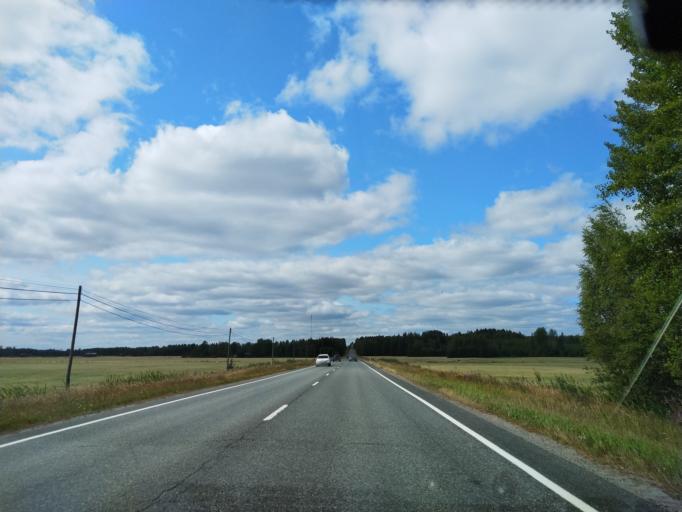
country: FI
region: Haeme
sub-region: Haemeenlinna
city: Tervakoski
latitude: 60.7401
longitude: 24.6194
